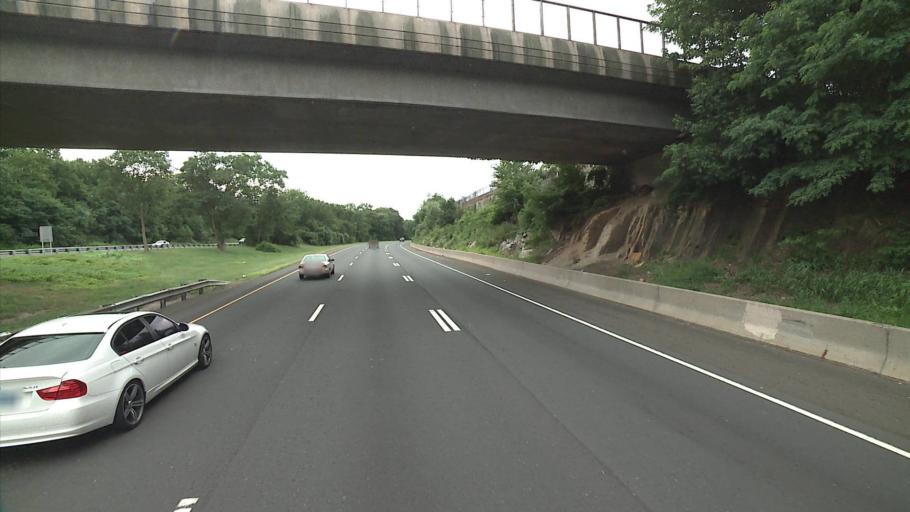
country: US
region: Connecticut
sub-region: Fairfield County
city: Shelton
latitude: 41.2946
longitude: -73.1059
